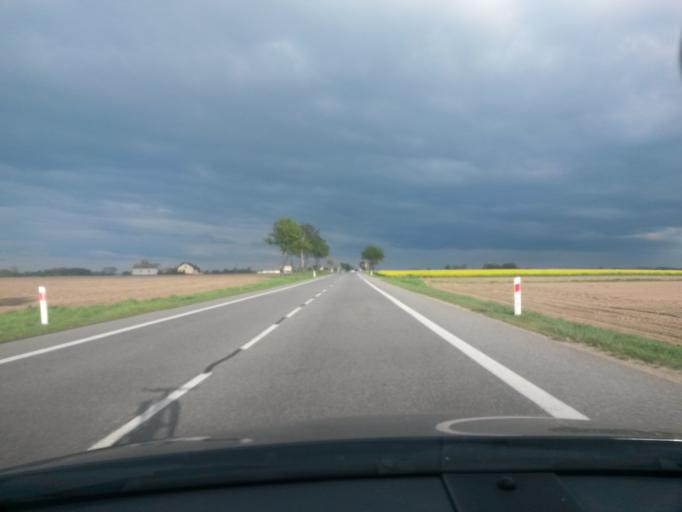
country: PL
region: Masovian Voivodeship
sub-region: Powiat plonski
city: Dzierzaznia
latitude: 52.6366
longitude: 20.1529
